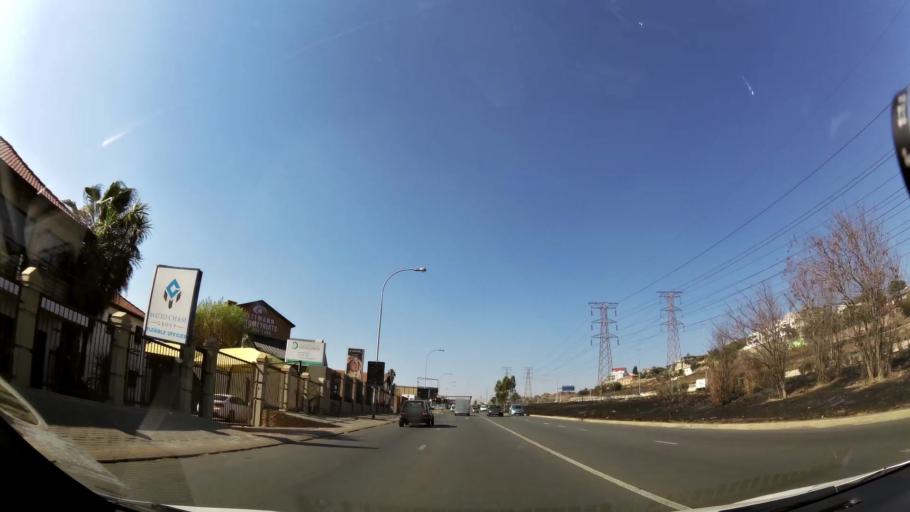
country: ZA
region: Gauteng
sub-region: City of Johannesburg Metropolitan Municipality
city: Johannesburg
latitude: -26.2686
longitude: 28.0550
